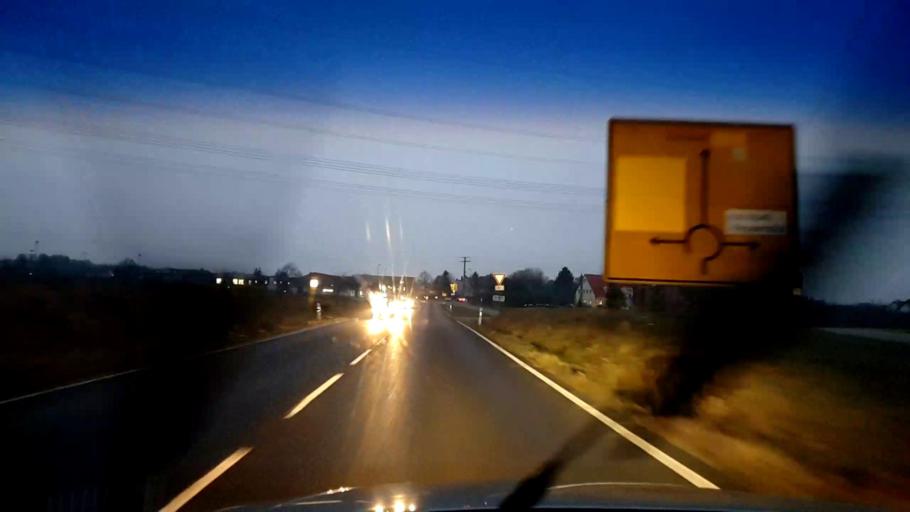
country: DE
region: Bavaria
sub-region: Upper Franconia
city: Hallstadt
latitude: 49.9362
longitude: 10.8826
